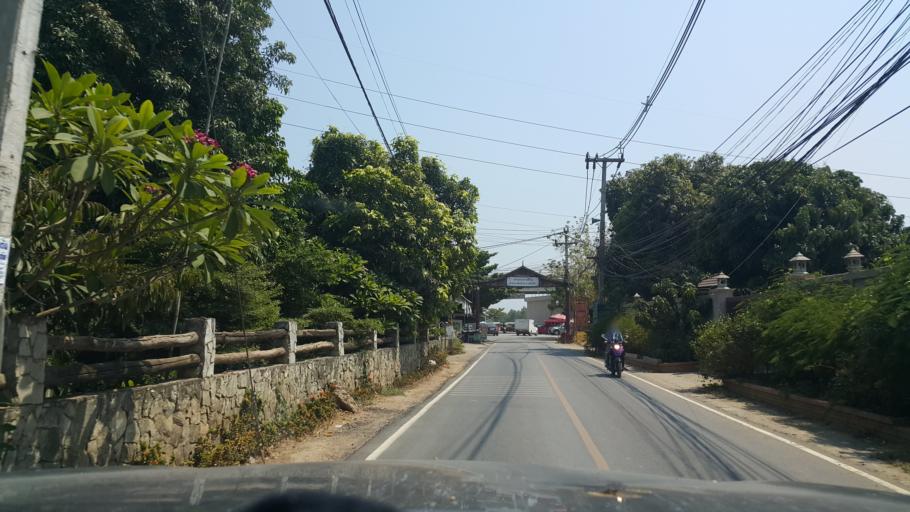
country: TH
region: Chiang Mai
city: Saraphi
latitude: 18.7210
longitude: 98.9879
